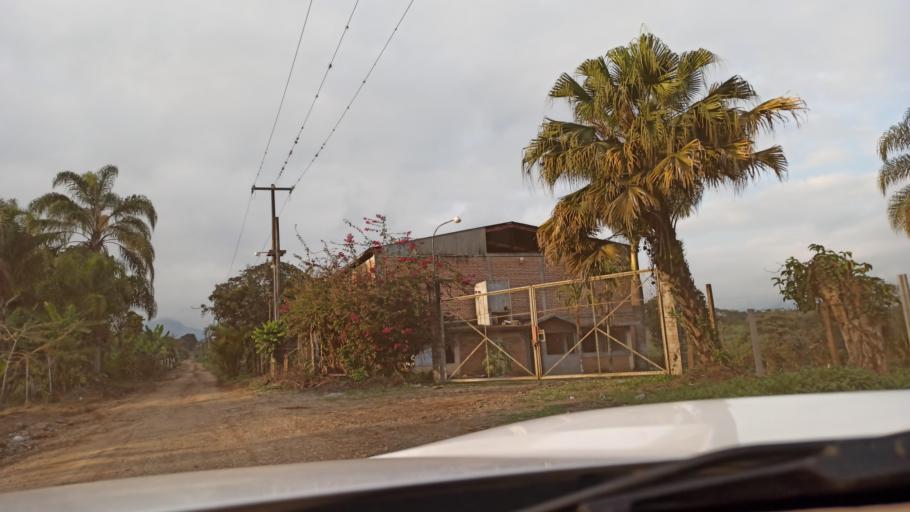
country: MX
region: Veracruz
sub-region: Fortin
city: Fortin de las Flores
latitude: 18.9192
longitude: -97.0037
